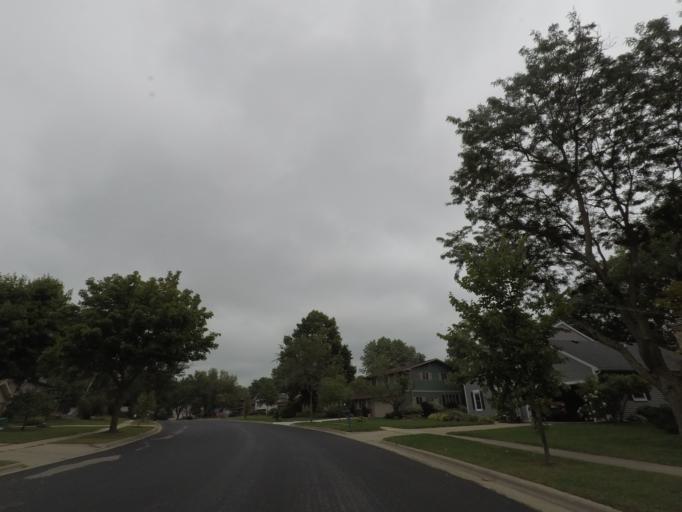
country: US
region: Wisconsin
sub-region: Dane County
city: Middleton
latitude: 43.0887
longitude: -89.5156
